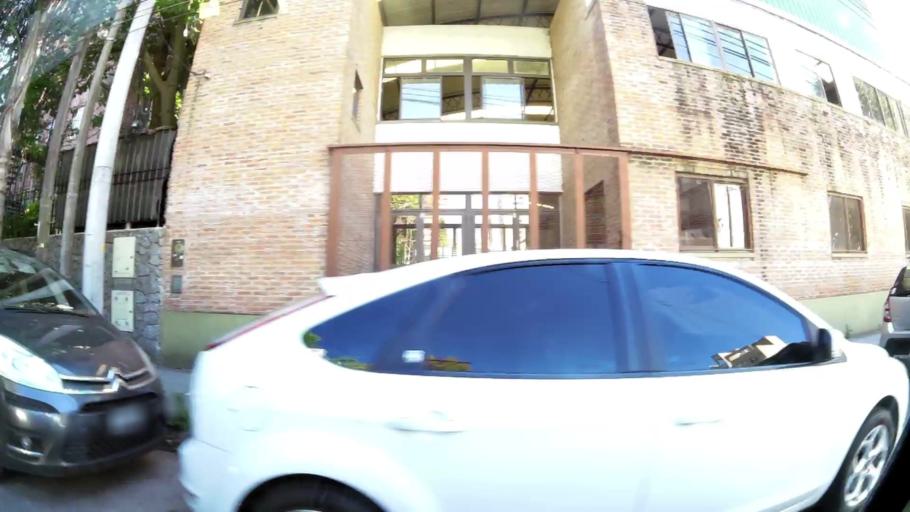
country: AR
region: Buenos Aires
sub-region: Partido de Vicente Lopez
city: Olivos
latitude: -34.5195
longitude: -58.4734
